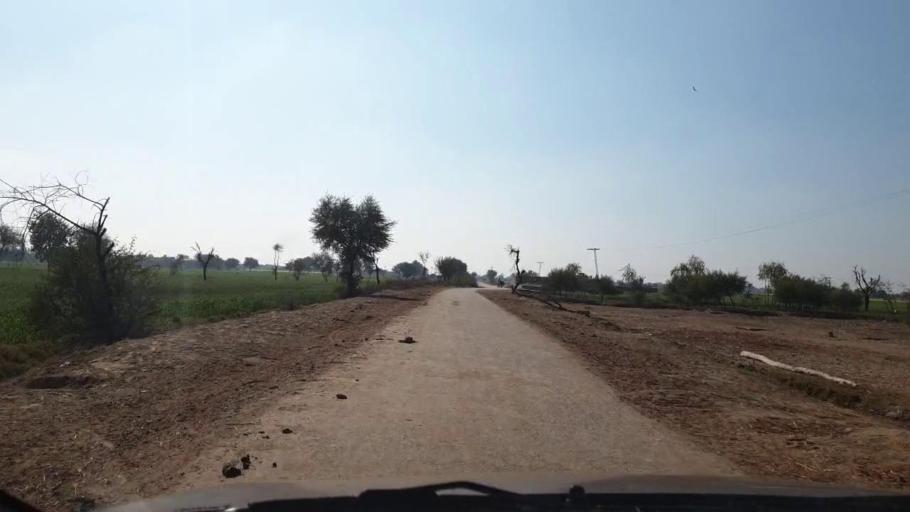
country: PK
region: Sindh
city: Sinjhoro
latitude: 25.9547
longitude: 68.7449
